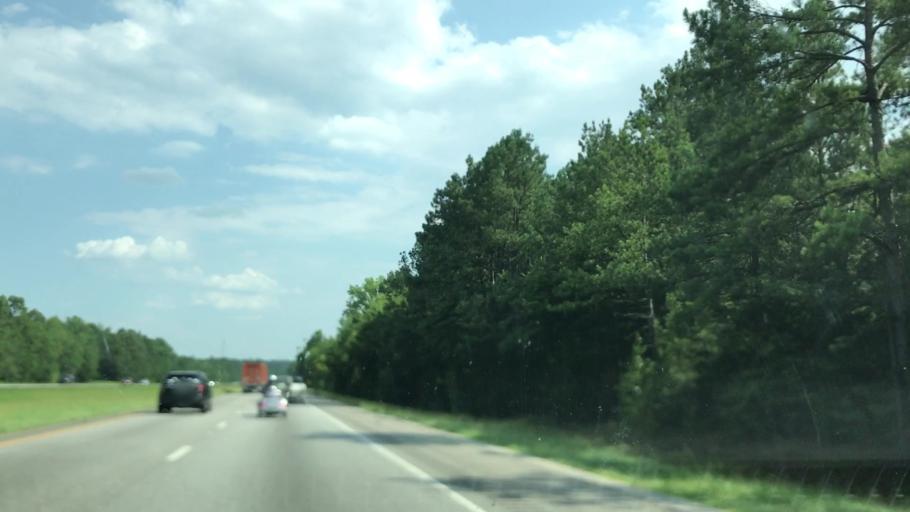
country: US
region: South Carolina
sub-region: Chester County
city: Great Falls
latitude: 34.6360
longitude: -81.0274
